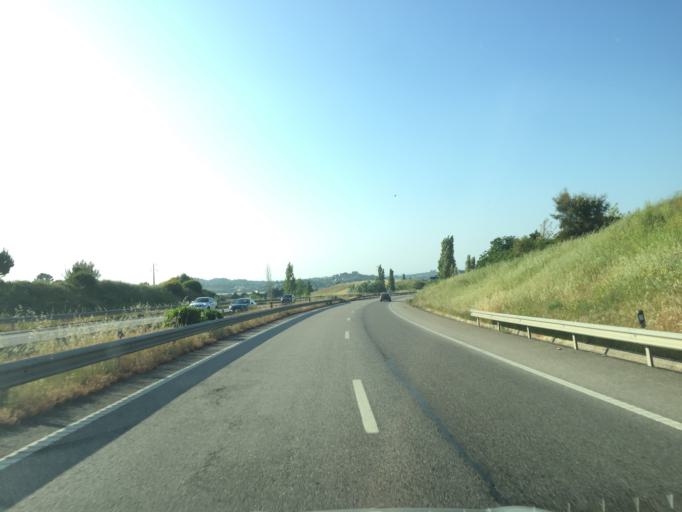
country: PT
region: Santarem
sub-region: Santarem
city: Santarem
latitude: 39.2121
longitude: -8.7018
